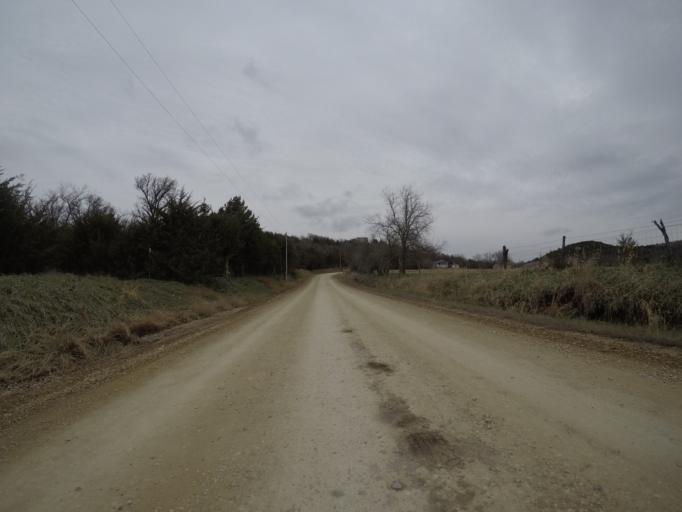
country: US
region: Kansas
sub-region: Riley County
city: Ogden
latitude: 39.1685
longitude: -96.6819
